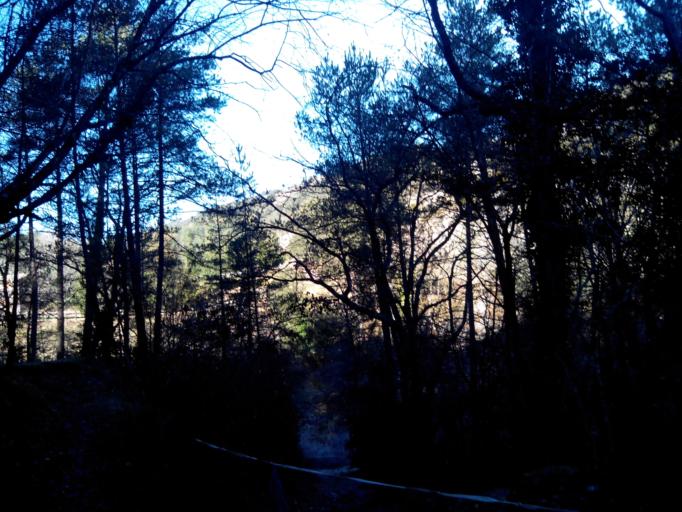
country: ES
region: Catalonia
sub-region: Provincia de Barcelona
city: Vilada
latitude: 42.1048
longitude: 1.9466
